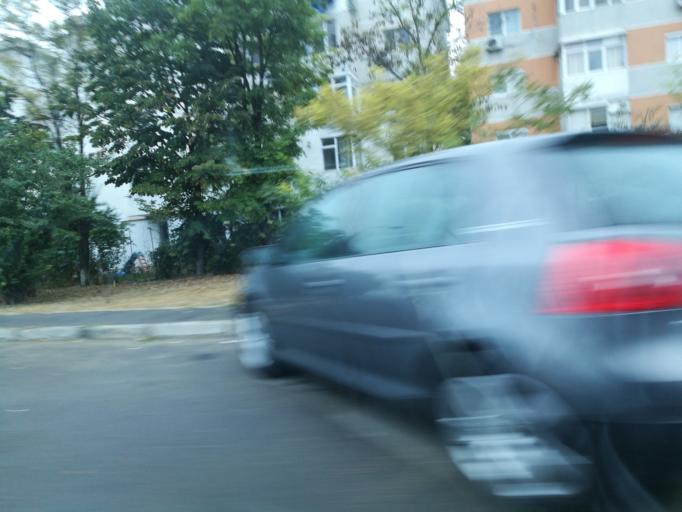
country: RO
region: Galati
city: Galati
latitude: 45.4530
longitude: 28.0140
